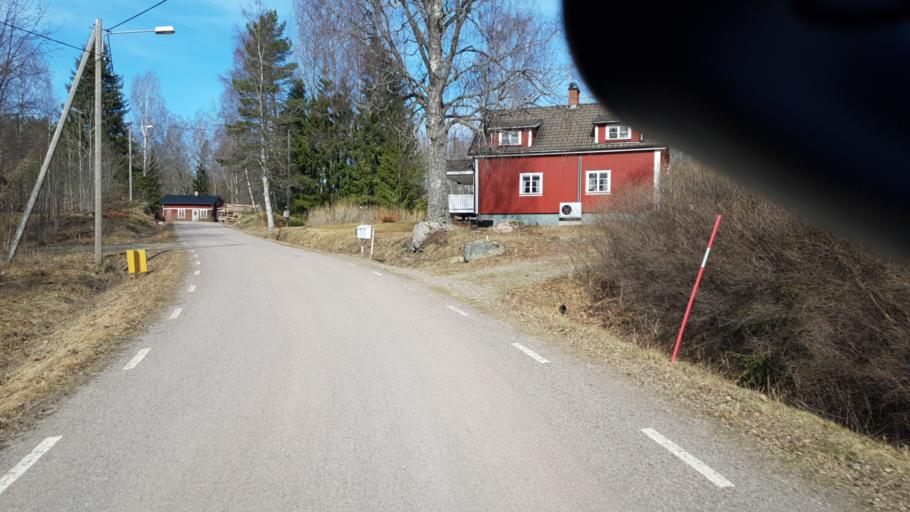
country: SE
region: Vaermland
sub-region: Arvika Kommun
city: Arvika
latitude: 59.5335
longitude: 12.4785
